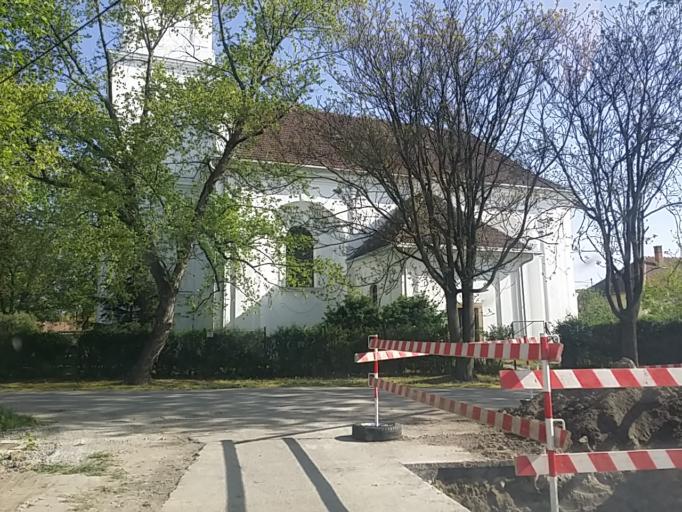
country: HU
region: Bekes
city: Doboz
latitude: 46.7357
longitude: 21.2468
